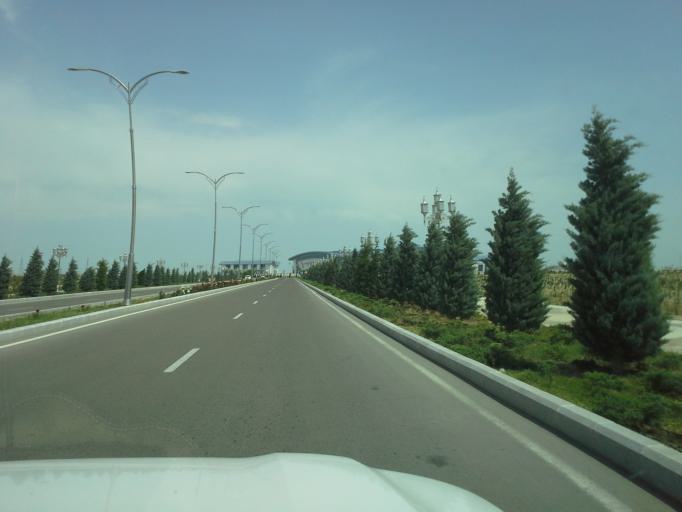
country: TM
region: Balkan
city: Turkmenbasy
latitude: 39.9677
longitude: 52.8456
